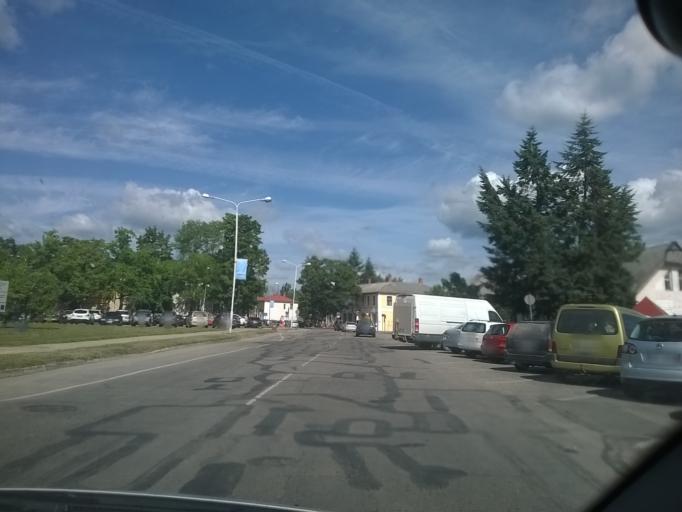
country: LV
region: Aluksnes Rajons
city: Aluksne
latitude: 57.4200
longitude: 27.0519
